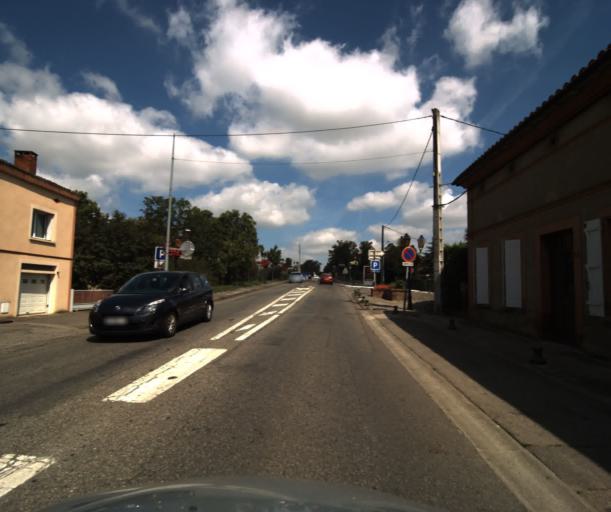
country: FR
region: Midi-Pyrenees
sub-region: Departement de la Haute-Garonne
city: Pinsaguel
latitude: 43.5106
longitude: 1.3886
